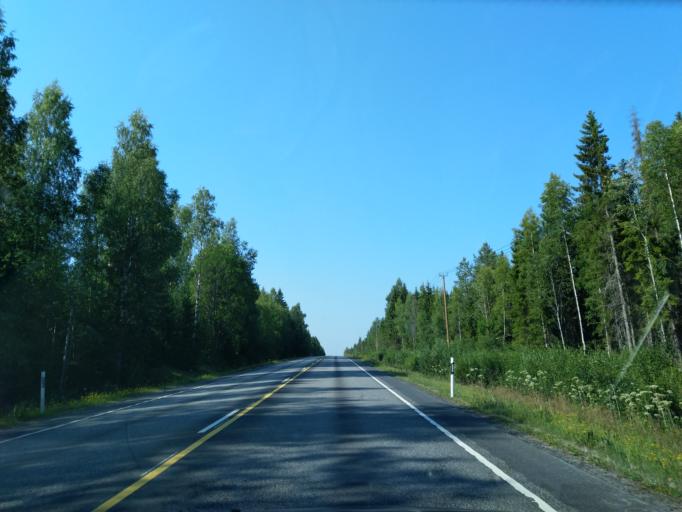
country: FI
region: Satakunta
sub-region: Pori
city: Pomarkku
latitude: 61.7251
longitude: 22.0616
